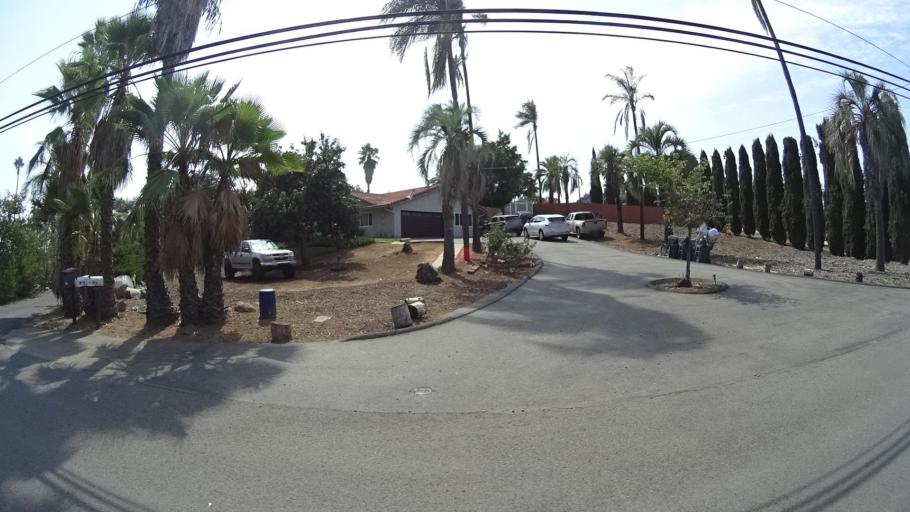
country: US
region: California
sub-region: San Diego County
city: Escondido
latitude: 33.1194
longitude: -117.0590
